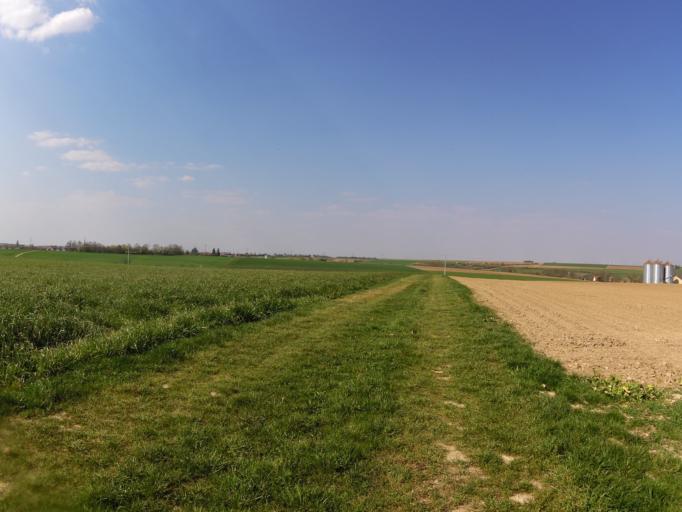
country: DE
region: Bavaria
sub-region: Regierungsbezirk Unterfranken
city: Mainstockheim
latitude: 49.8166
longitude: 10.1197
